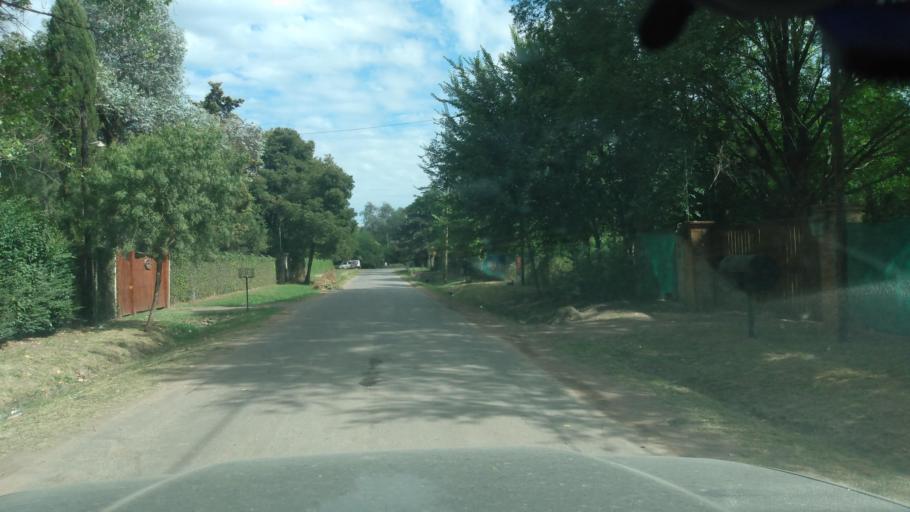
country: AR
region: Buenos Aires
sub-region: Partido de Lujan
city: Lujan
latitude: -34.5889
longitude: -59.0510
